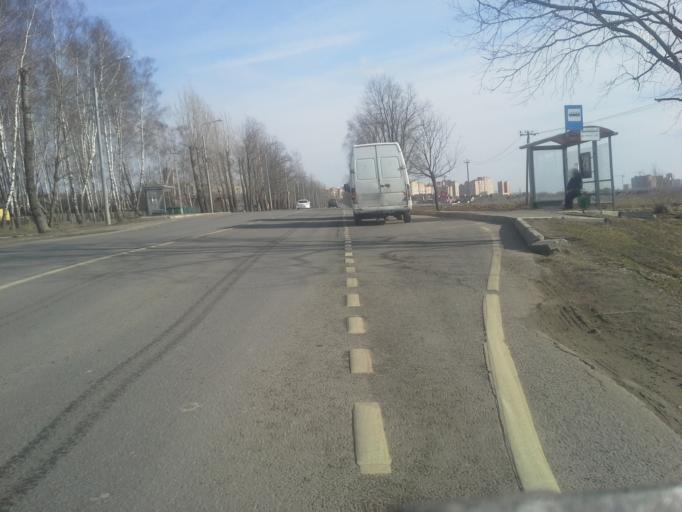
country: RU
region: Moskovskaya
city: Shcherbinka
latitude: 55.4789
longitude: 37.5266
